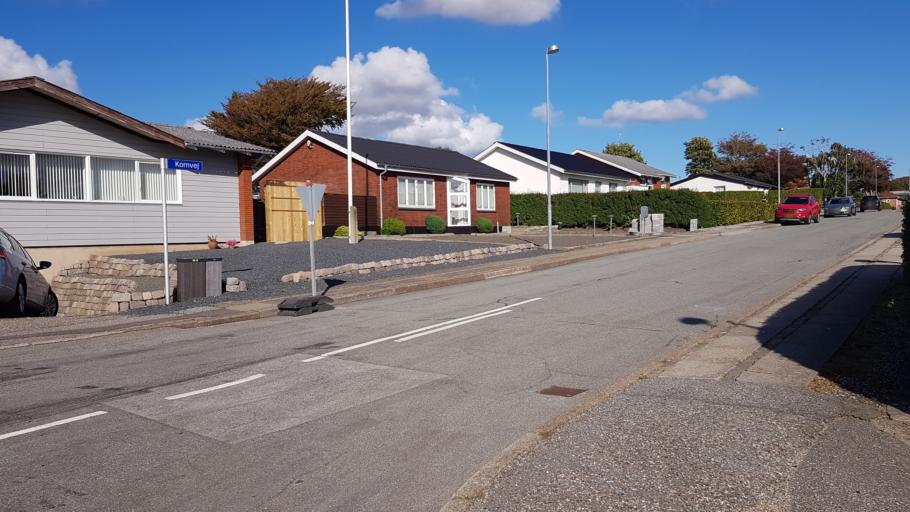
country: DK
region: North Denmark
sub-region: Thisted Kommune
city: Thisted
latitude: 56.9597
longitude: 8.6954
